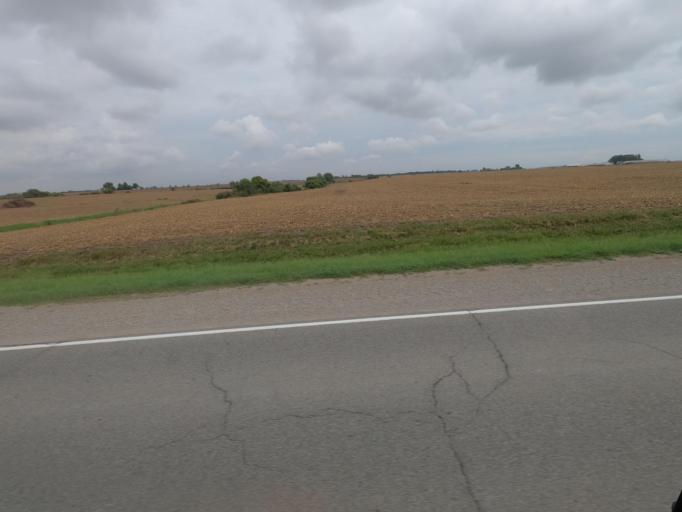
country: US
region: Iowa
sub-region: Wapello County
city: Ottumwa
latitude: 40.9565
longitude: -92.2365
